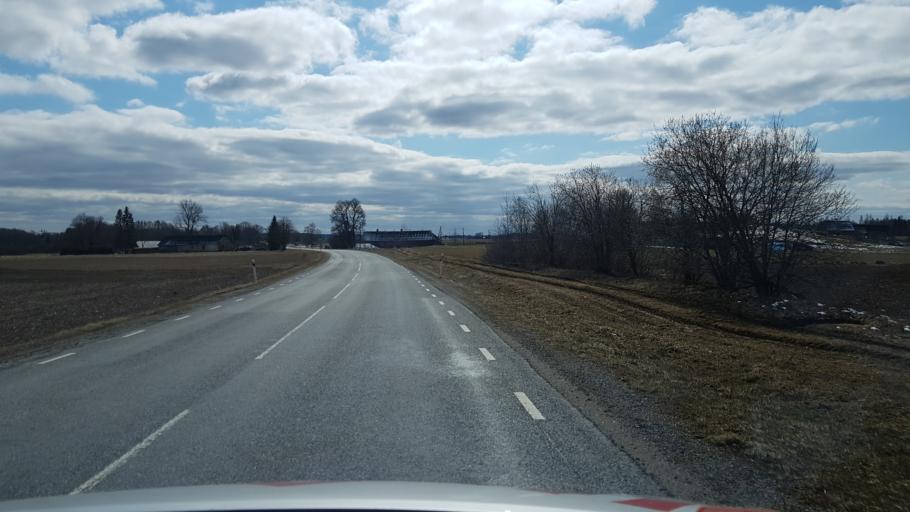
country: EE
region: Laeaene-Virumaa
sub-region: Tapa vald
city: Tapa
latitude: 59.3299
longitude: 26.0003
